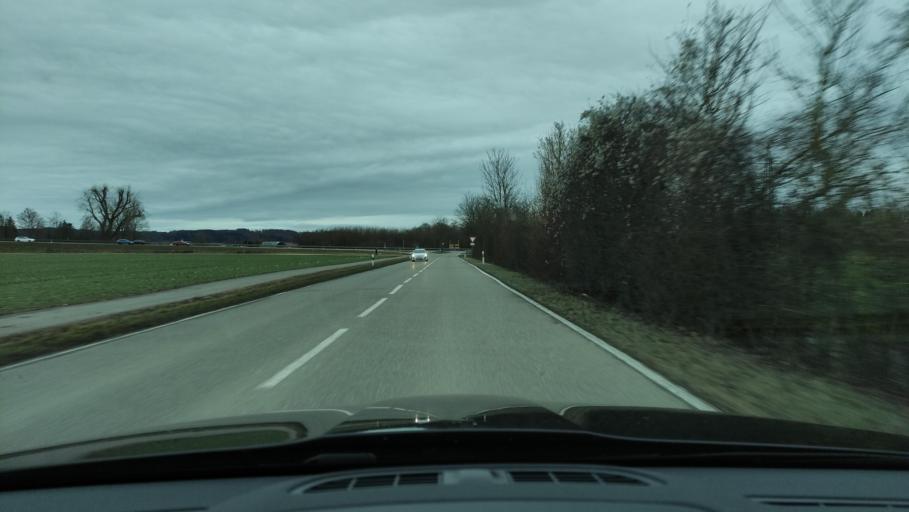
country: DE
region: Bavaria
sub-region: Swabia
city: Illertissen
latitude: 48.2078
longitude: 10.0940
